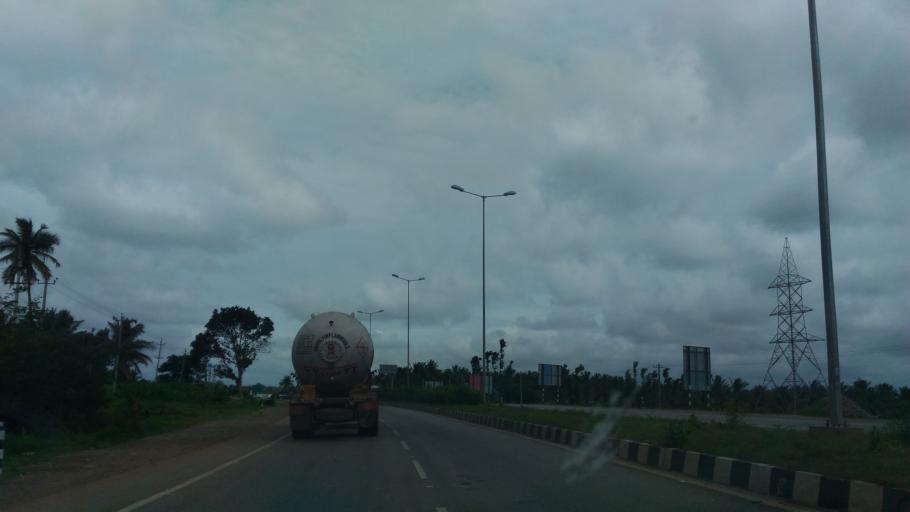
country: IN
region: Karnataka
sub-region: Hassan
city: Hassan
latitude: 12.9840
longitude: 76.2269
